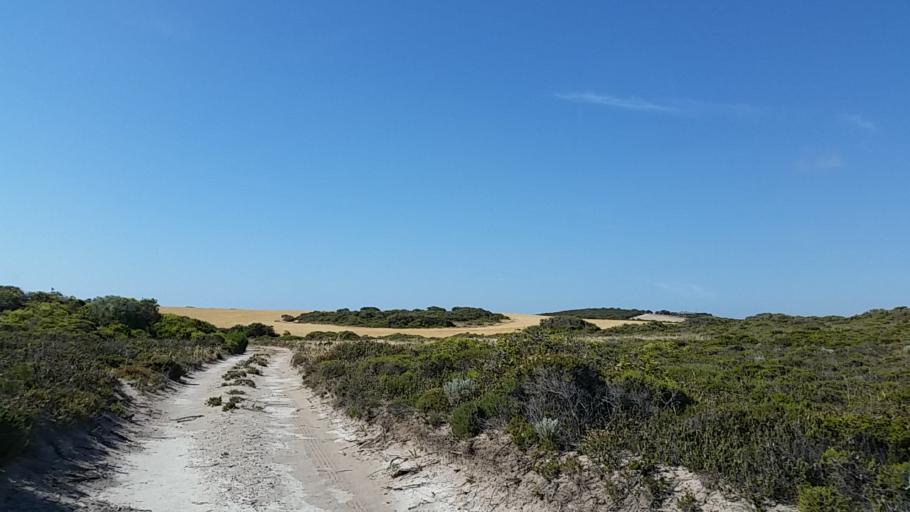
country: AU
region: South Australia
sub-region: Yorke Peninsula
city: Honiton
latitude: -35.2376
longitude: 137.1516
